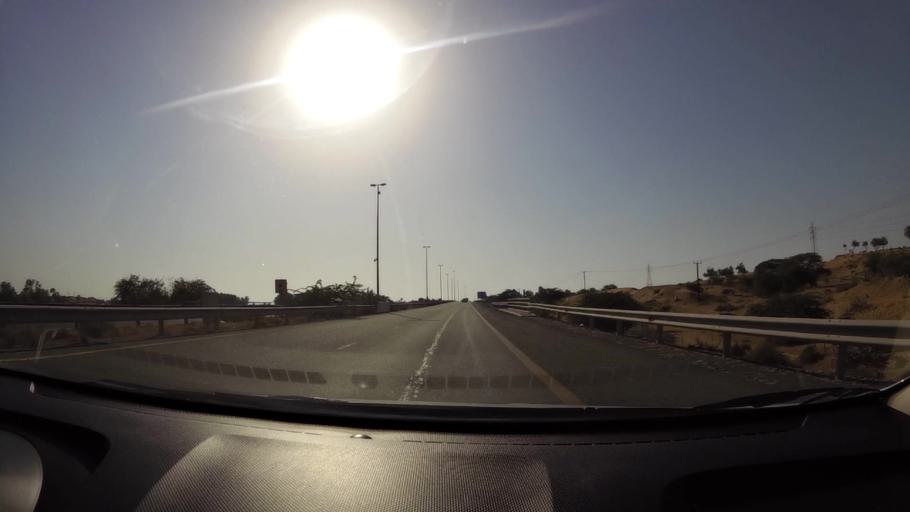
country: AE
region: Umm al Qaywayn
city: Umm al Qaywayn
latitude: 25.4455
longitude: 55.6249
